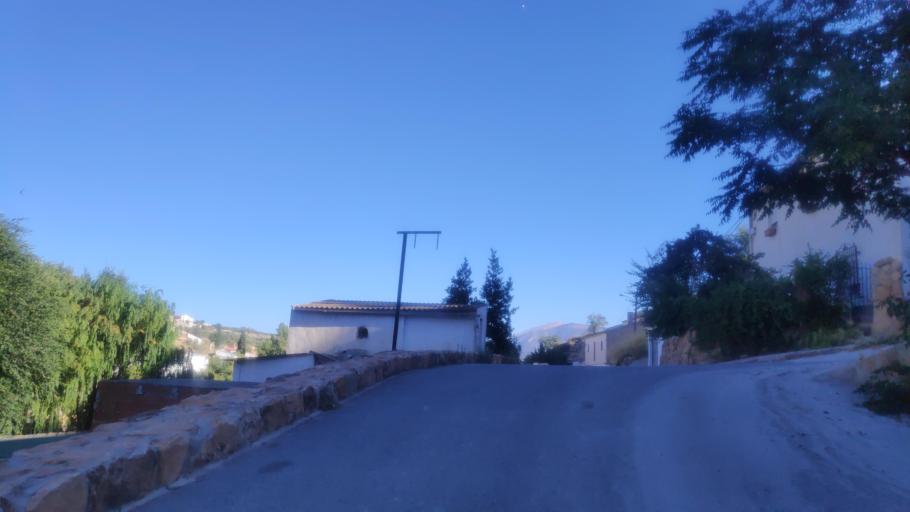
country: ES
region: Andalusia
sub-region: Provincia de Jaen
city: Pozo Alcon
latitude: 37.6750
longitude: -2.9726
